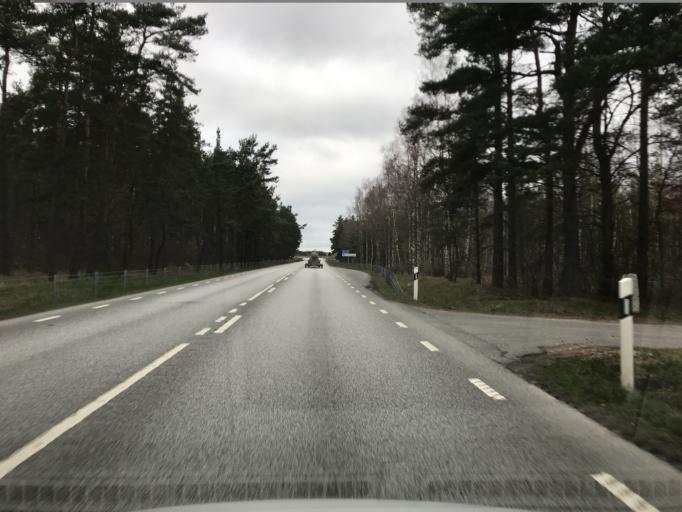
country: SE
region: Skane
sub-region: Kristianstads Kommun
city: Norra Asum
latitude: 55.9422
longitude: 14.0698
